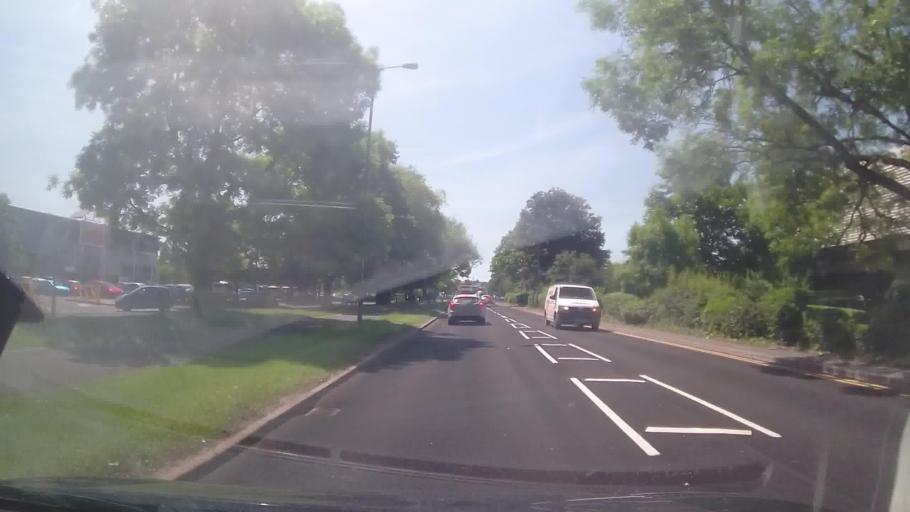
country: GB
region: England
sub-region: Herefordshire
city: Hereford
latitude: 52.0699
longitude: -2.7223
